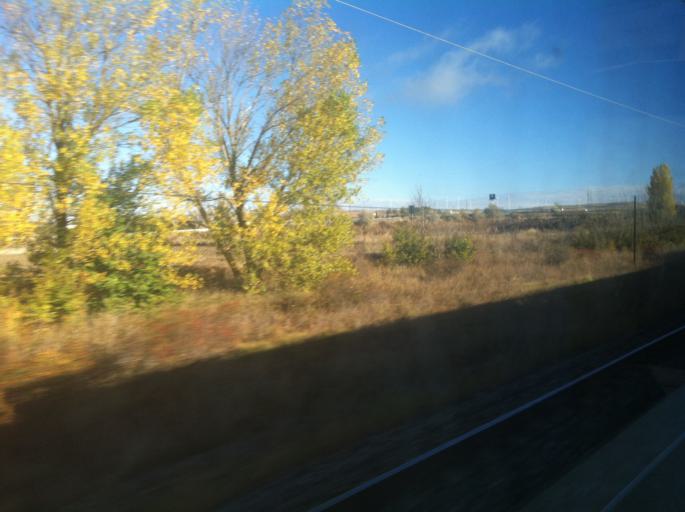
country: ES
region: Castille and Leon
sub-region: Provincia de Burgos
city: Villaverde-Mogina
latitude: 42.1722
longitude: -4.0624
